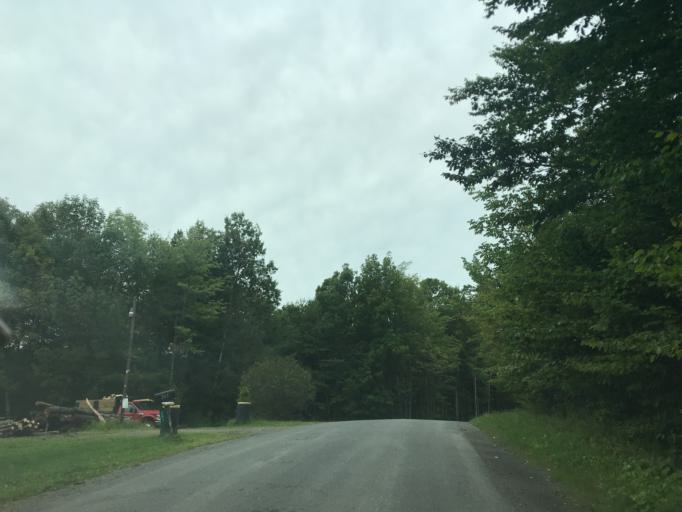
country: US
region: New York
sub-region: Otsego County
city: Worcester
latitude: 42.5283
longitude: -74.6619
